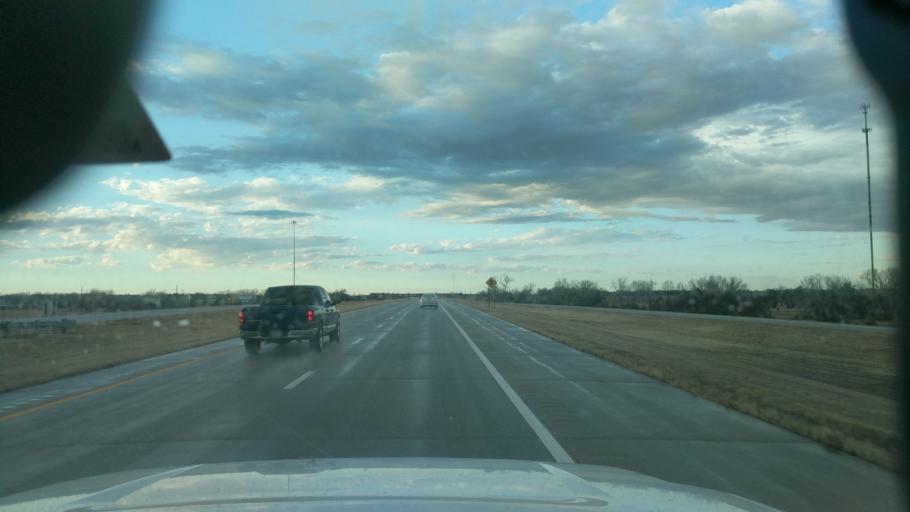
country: US
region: Kansas
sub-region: Harvey County
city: Hesston
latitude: 38.1453
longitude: -97.4179
